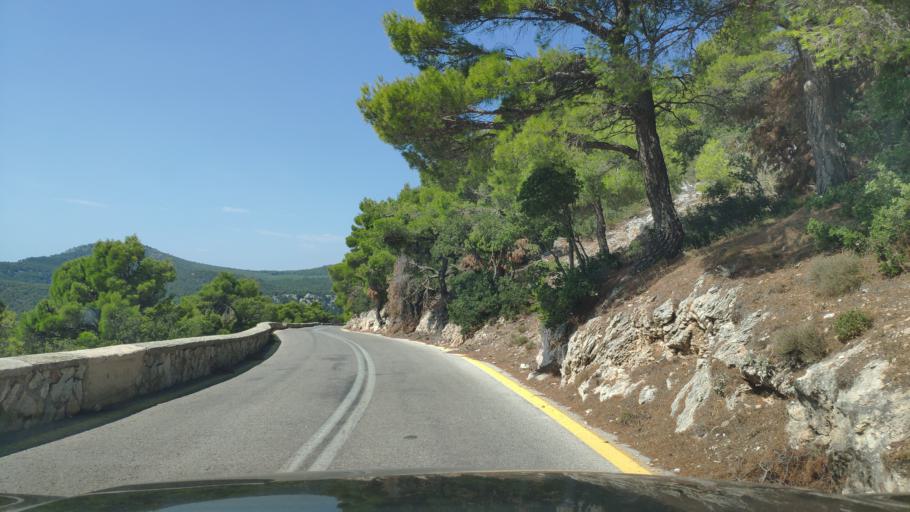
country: GR
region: Attica
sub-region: Nomarchia Anatolikis Attikis
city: Thrakomakedones
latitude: 38.1414
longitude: 23.7196
